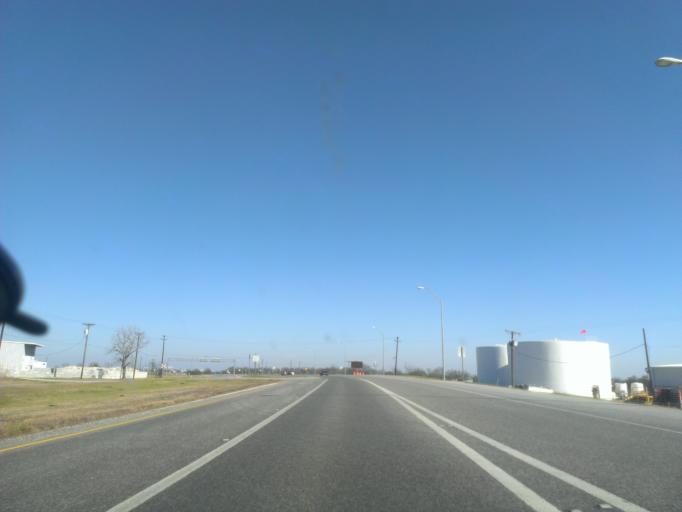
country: US
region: Texas
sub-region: Williamson County
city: Taylor
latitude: 30.5739
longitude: -97.3798
